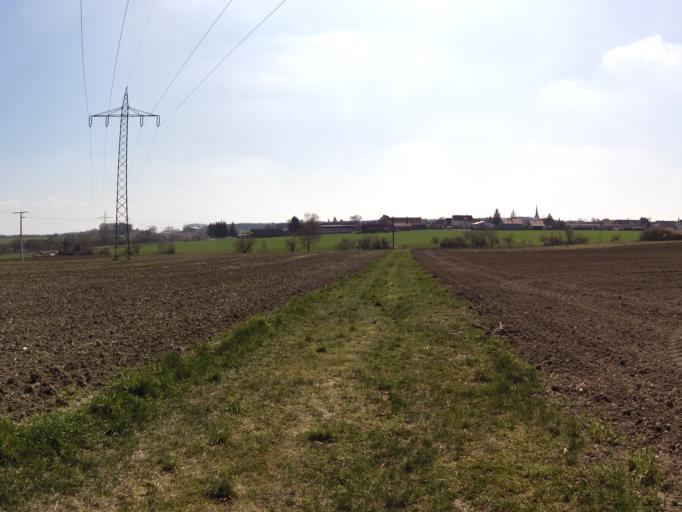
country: DE
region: Bavaria
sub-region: Regierungsbezirk Unterfranken
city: Biebelried
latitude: 49.7357
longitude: 10.0904
